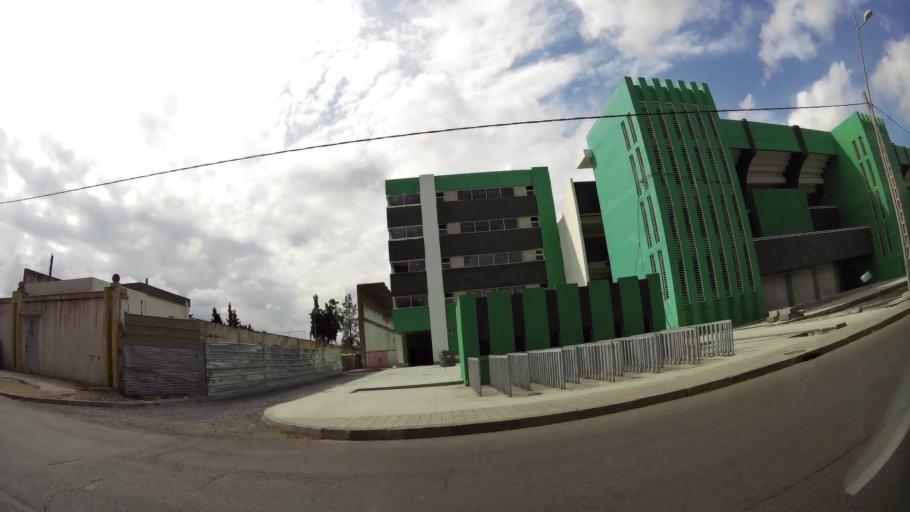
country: MA
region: Gharb-Chrarda-Beni Hssen
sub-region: Kenitra Province
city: Kenitra
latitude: 34.2539
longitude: -6.5715
